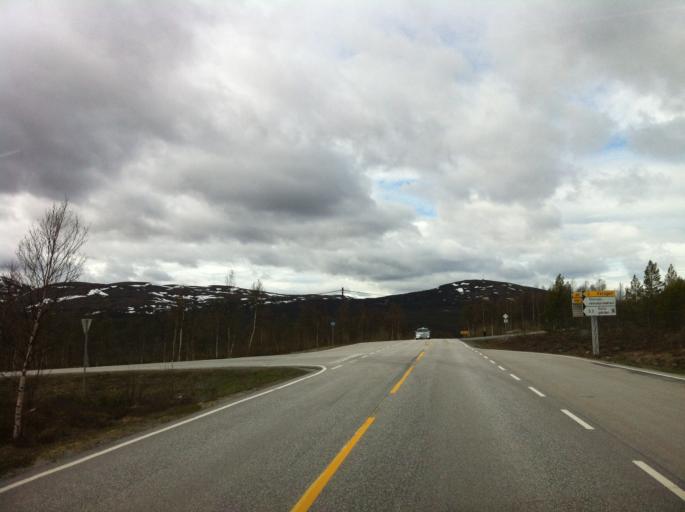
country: NO
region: Sor-Trondelag
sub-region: Roros
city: Roros
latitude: 62.5972
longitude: 11.8279
